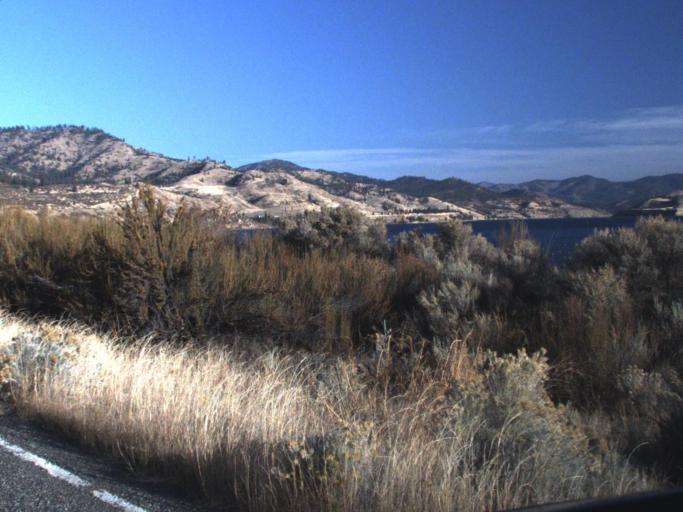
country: US
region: Washington
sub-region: Okanogan County
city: Coulee Dam
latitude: 47.9557
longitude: -118.6941
